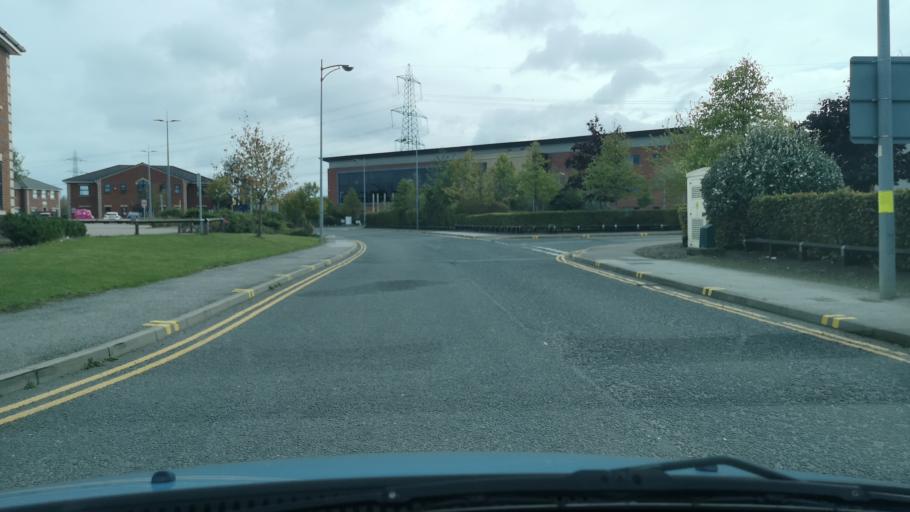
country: GB
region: England
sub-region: City and Borough of Wakefield
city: Castleford
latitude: 53.7073
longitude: -1.3420
